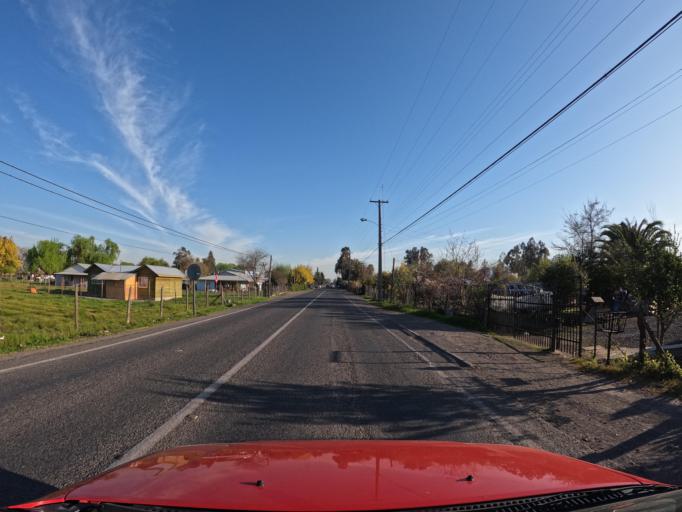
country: CL
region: Maule
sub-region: Provincia de Curico
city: Rauco
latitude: -34.8701
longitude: -71.2653
